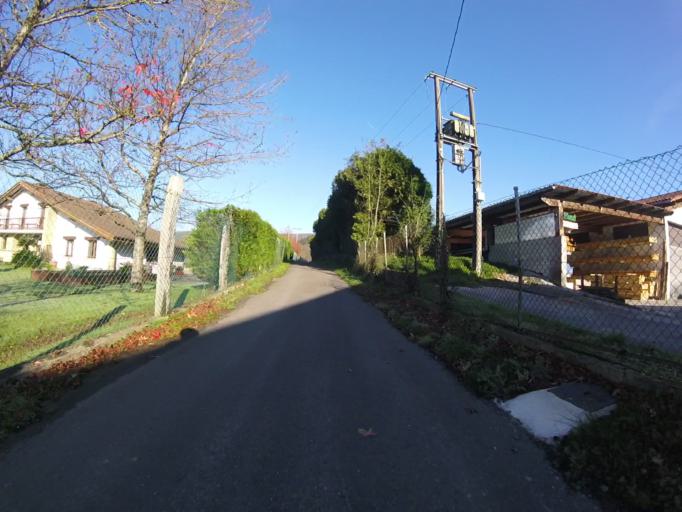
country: ES
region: Basque Country
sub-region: Provincia de Guipuzcoa
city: Usurbil
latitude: 43.2755
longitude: -2.0689
